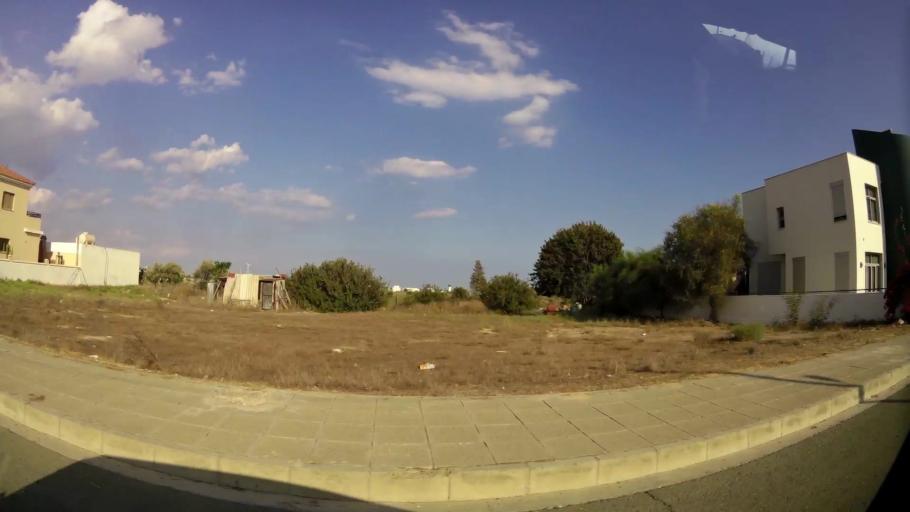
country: CY
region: Larnaka
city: Dhromolaxia
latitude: 34.8732
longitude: 33.5972
